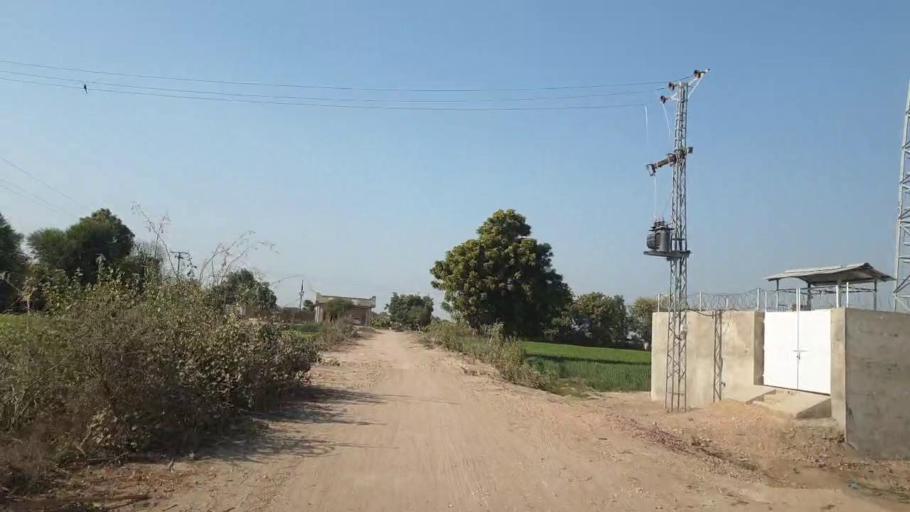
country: PK
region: Sindh
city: Tando Allahyar
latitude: 25.5698
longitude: 68.7088
